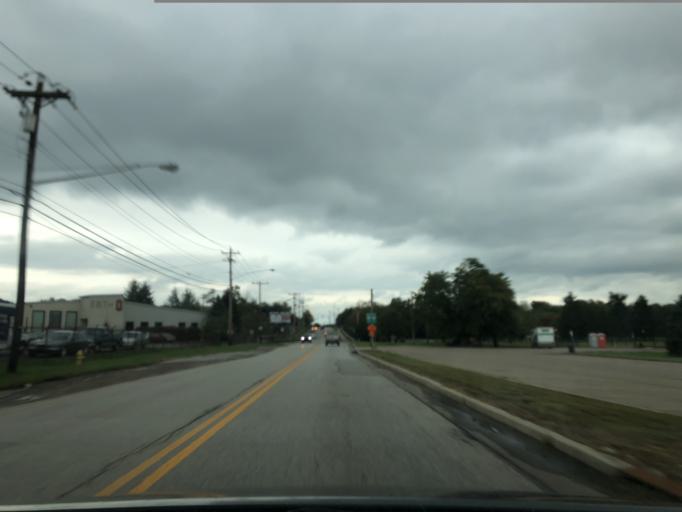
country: US
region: Ohio
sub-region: Hamilton County
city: Turpin Hills
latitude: 39.1151
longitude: -84.4169
